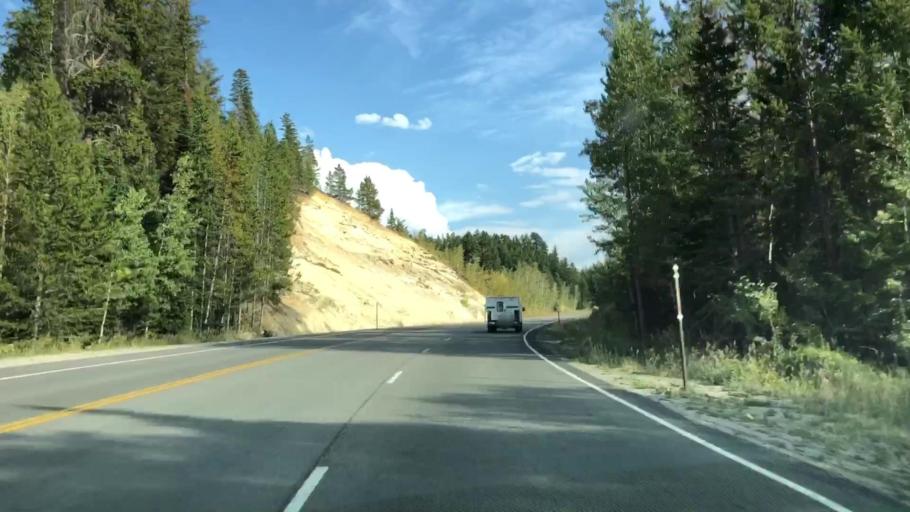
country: US
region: Wyoming
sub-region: Sublette County
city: Pinedale
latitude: 43.1373
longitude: -110.2088
